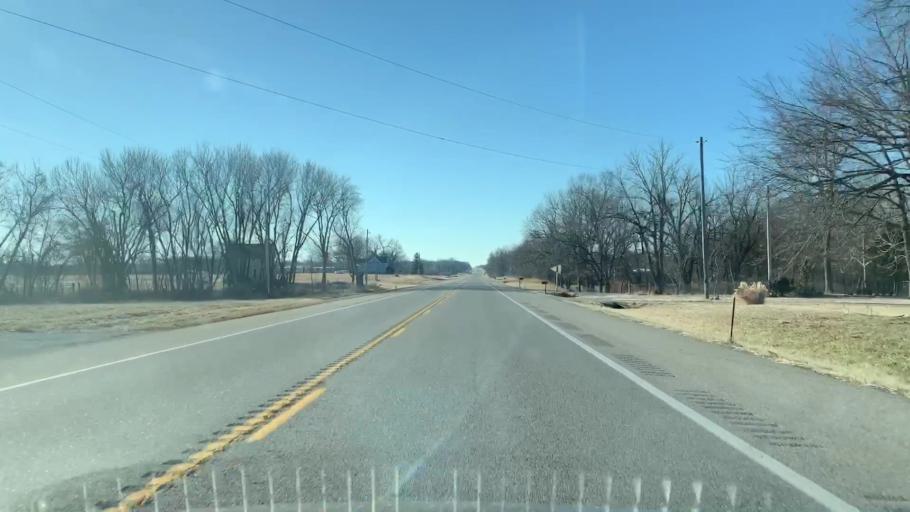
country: US
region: Kansas
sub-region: Crawford County
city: Pittsburg
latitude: 37.3183
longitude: -94.7055
